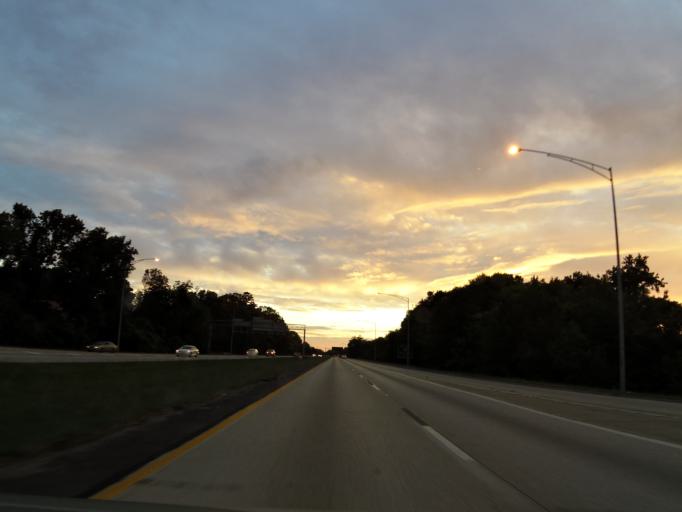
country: US
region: Alabama
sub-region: Jefferson County
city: Irondale
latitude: 33.5804
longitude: -86.7090
